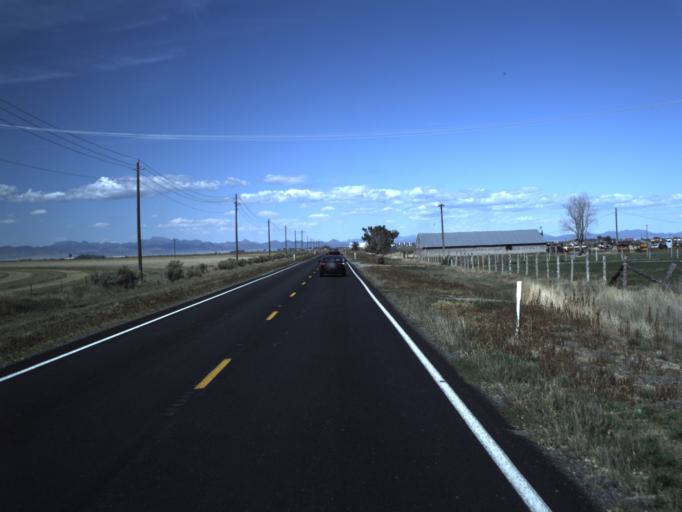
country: US
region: Utah
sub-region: Washington County
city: Enterprise
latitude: 37.6590
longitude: -113.6612
